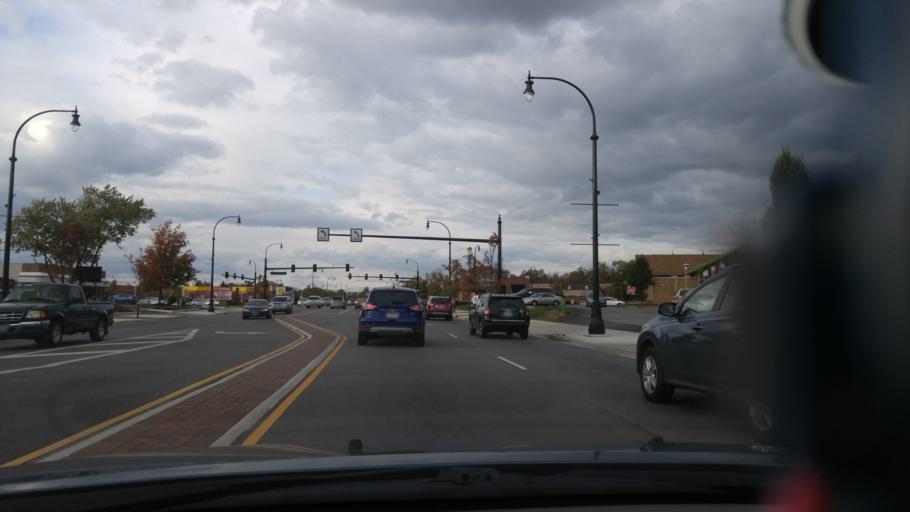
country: US
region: Ohio
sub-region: Franklin County
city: Westerville
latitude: 40.1086
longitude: -82.9251
